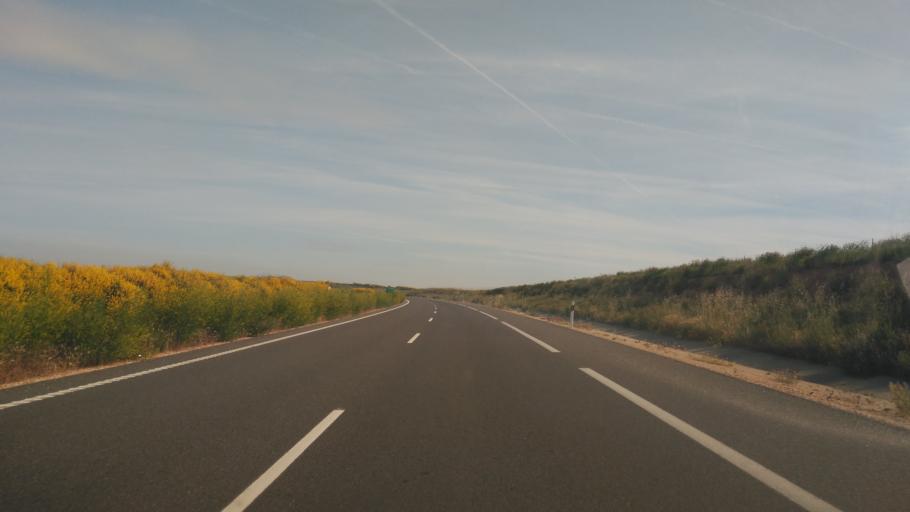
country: ES
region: Castille and Leon
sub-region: Provincia de Salamanca
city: Castellanos de Villiquera
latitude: 41.0445
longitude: -5.6672
